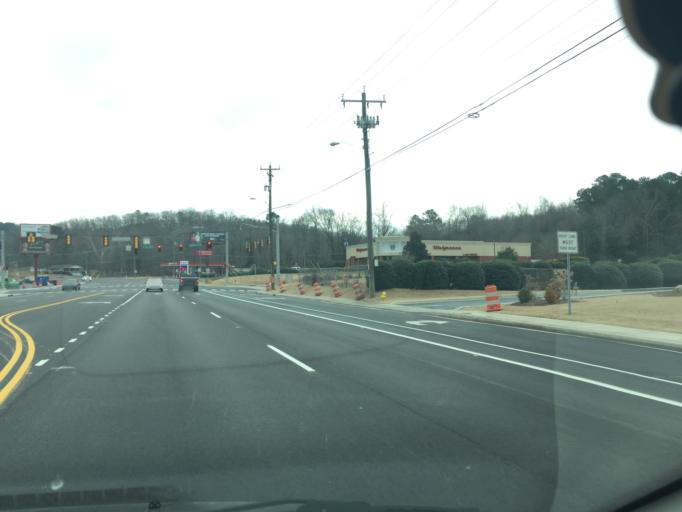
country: US
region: Tennessee
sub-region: Hamilton County
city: East Brainerd
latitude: 35.0010
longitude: -85.1338
